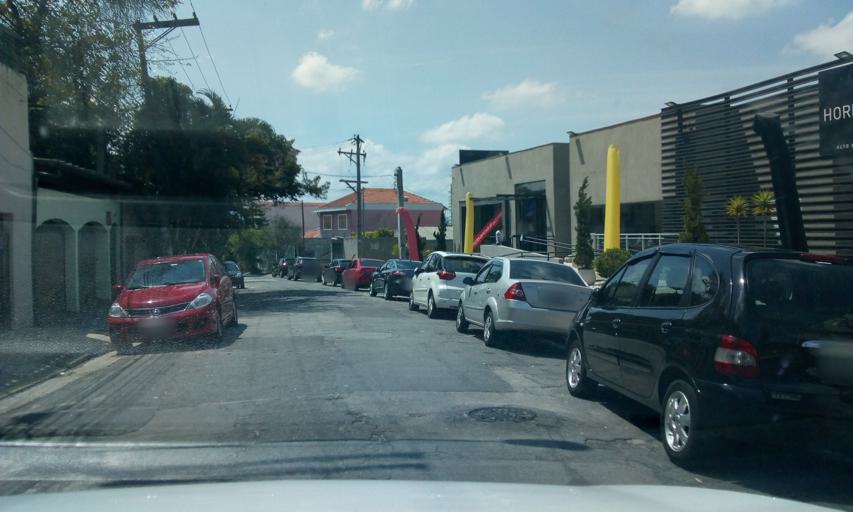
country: BR
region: Sao Paulo
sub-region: Sao Paulo
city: Sao Paulo
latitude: -23.5353
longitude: -46.7080
